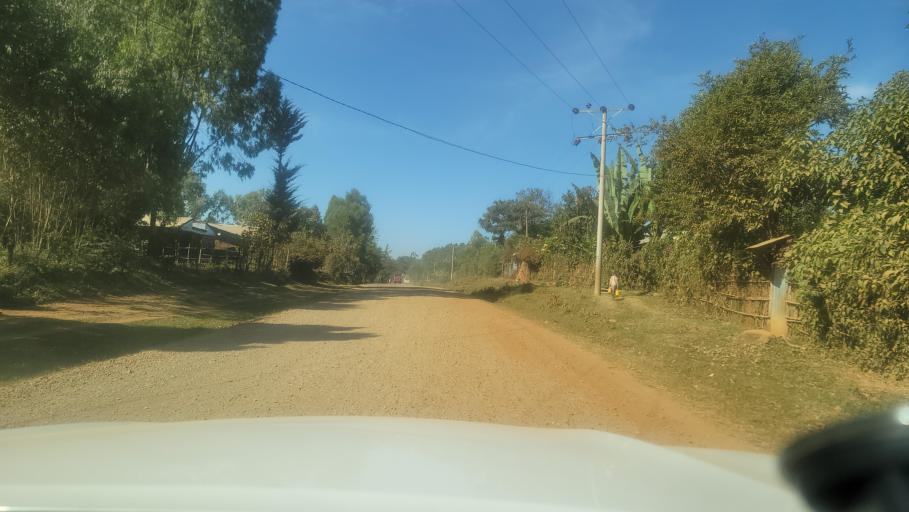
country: ET
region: Oromiya
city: Agaro
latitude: 7.7975
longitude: 36.4879
